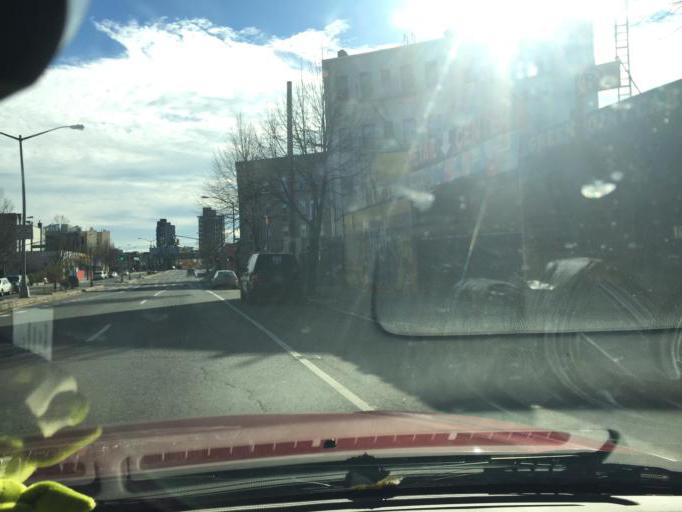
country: US
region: New York
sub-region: Queens County
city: Long Island City
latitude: 40.7222
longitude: -73.9465
